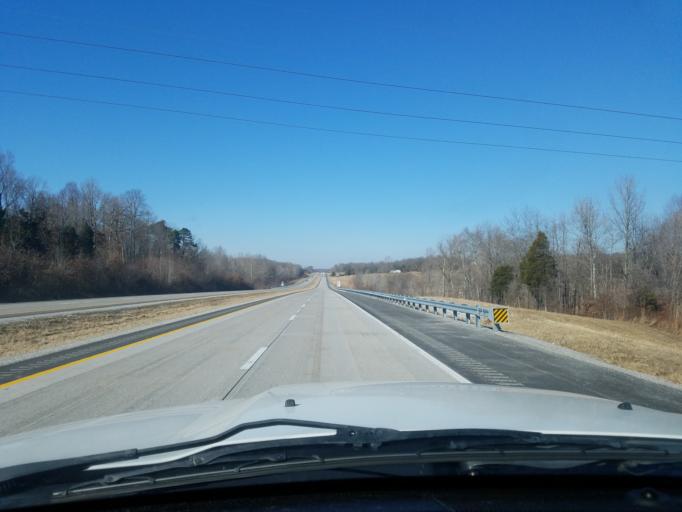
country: US
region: Kentucky
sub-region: Ohio County
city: Beaver Dam
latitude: 37.3997
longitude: -86.8198
